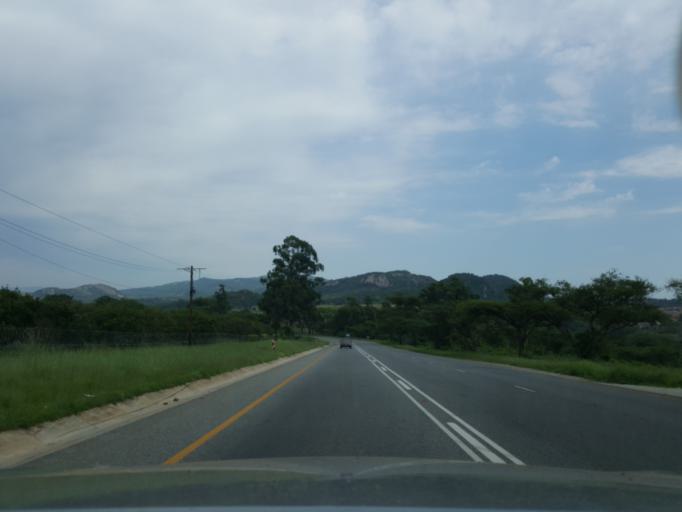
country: ZA
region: Mpumalanga
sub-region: Ehlanzeni District
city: Nelspruit
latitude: -25.4764
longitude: 31.1055
